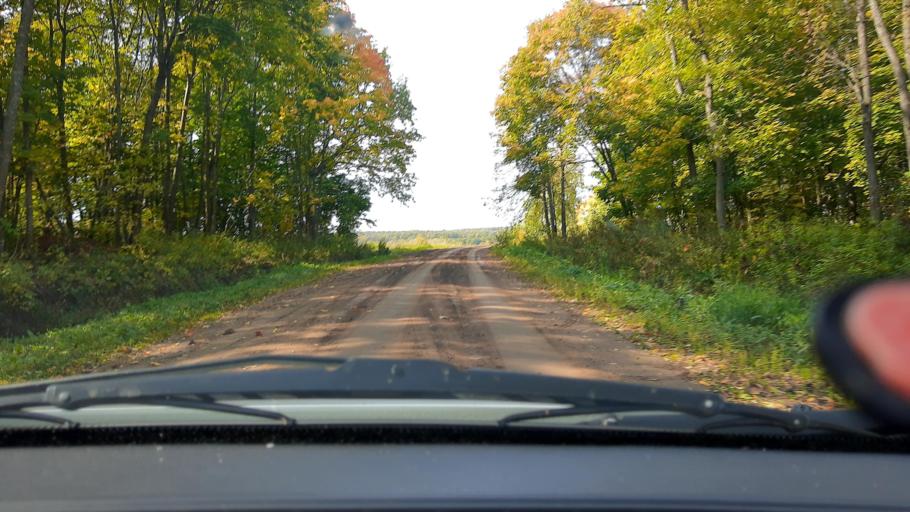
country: RU
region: Bashkortostan
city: Kudeyevskiy
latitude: 54.7122
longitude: 56.6425
